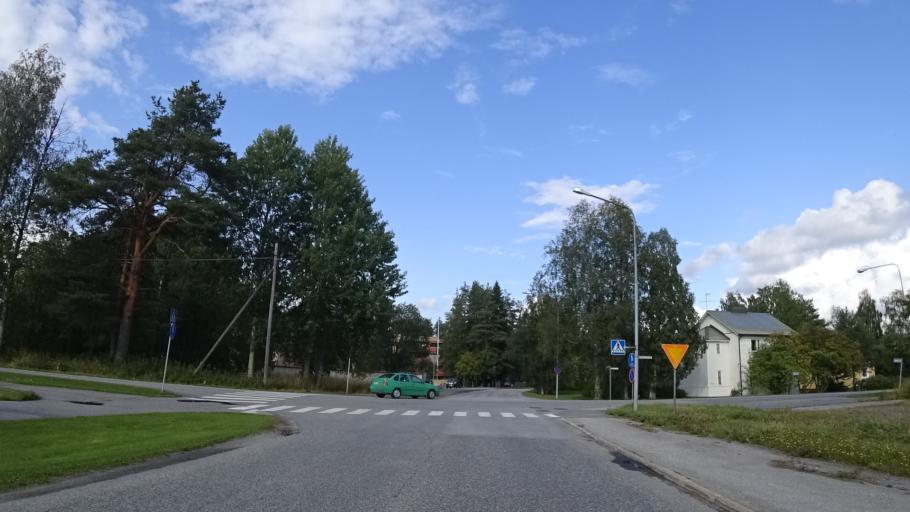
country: FI
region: North Karelia
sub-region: Pielisen Karjala
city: Lieksa
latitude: 63.3231
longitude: 30.0110
